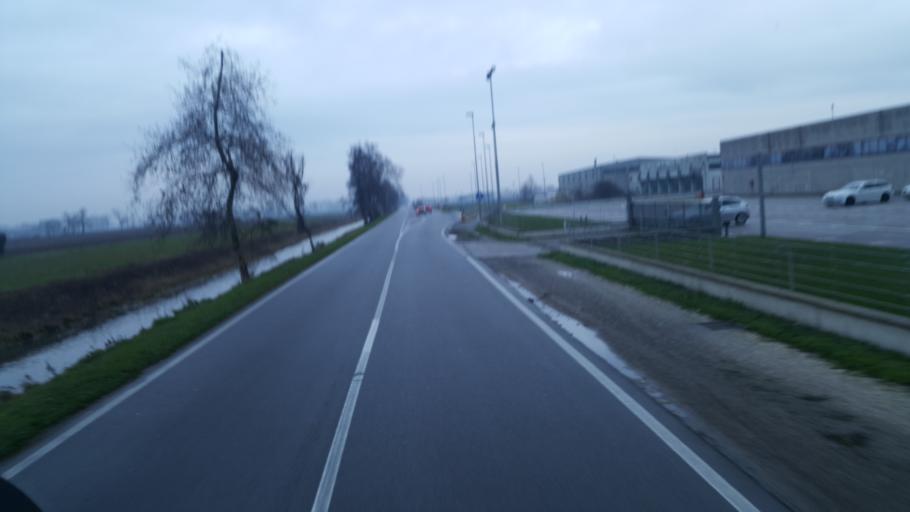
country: IT
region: Lombardy
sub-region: Provincia di Mantova
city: Casalmoro
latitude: 45.2659
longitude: 10.4144
